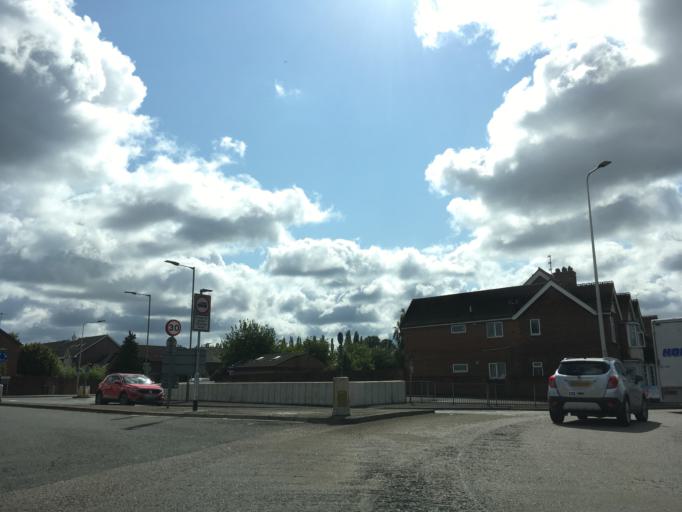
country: GB
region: England
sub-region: West Berkshire
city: Newbury
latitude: 51.3965
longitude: -1.3202
